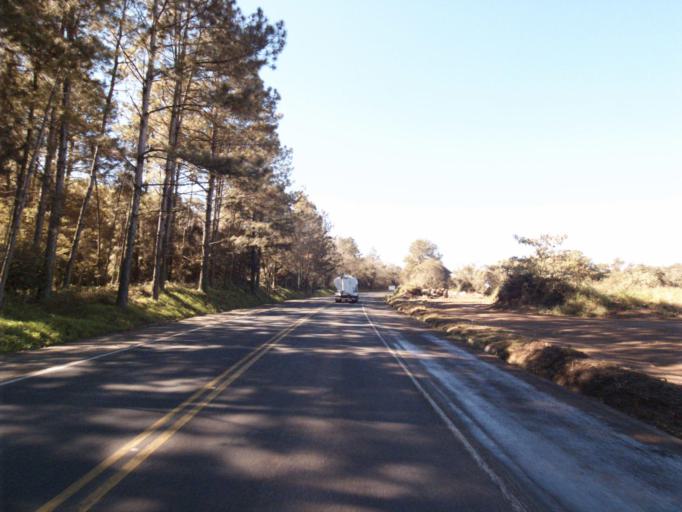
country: BR
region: Santa Catarina
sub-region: Sao Lourenco Do Oeste
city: Sao Lourenco dOeste
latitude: -26.8256
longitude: -53.0862
